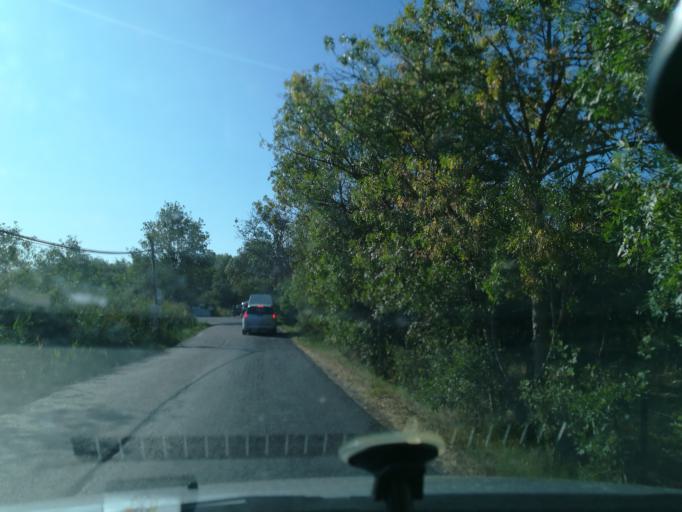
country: FR
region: Languedoc-Roussillon
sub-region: Departement de l'Herault
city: Portiragnes
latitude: 43.2894
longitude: 3.3642
